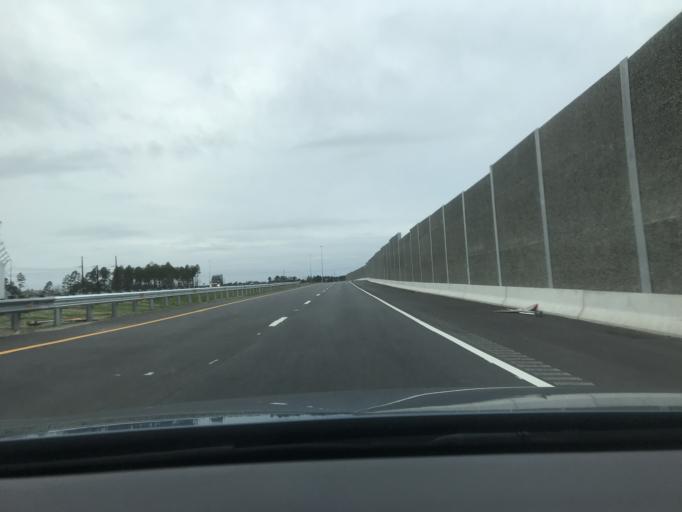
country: US
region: North Carolina
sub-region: Cumberland County
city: Fort Bragg
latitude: 35.1074
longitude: -79.0043
